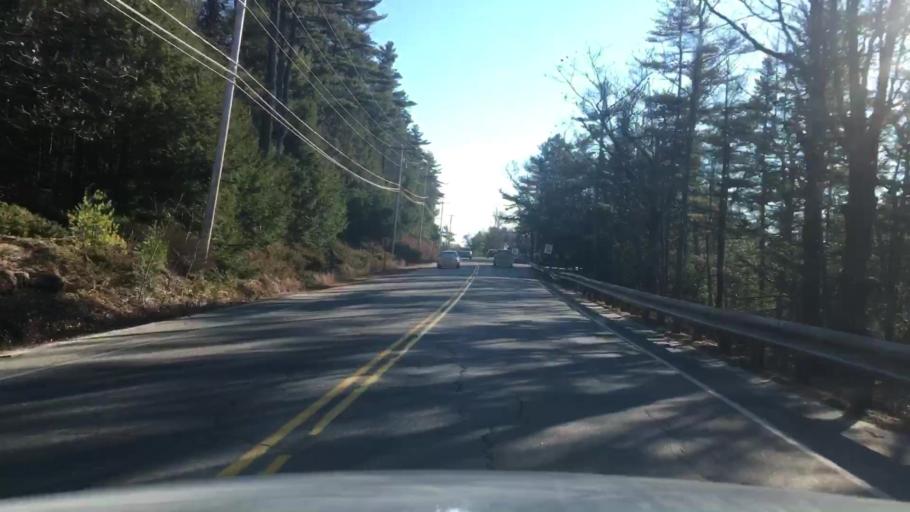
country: US
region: Maine
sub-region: Cumberland County
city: Brunswick
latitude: 43.8672
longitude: -69.9141
